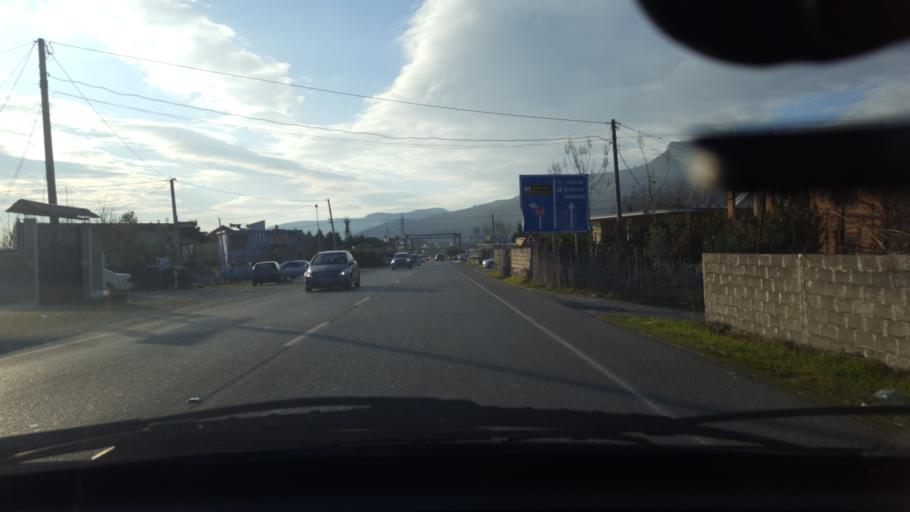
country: AL
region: Elbasan
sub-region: Rrethi i Elbasanit
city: Bradashesh
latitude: 41.0991
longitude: 20.0398
